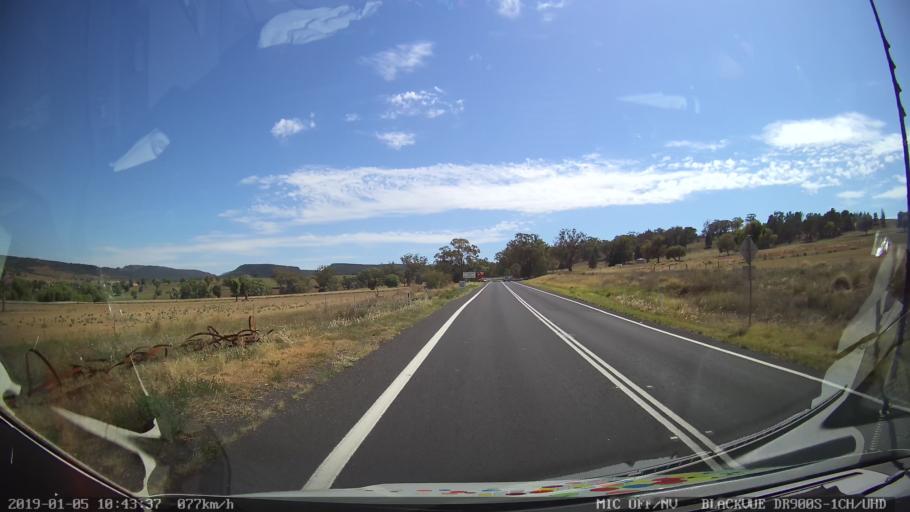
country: AU
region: New South Wales
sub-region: Warrumbungle Shire
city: Coonabarabran
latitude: -31.4627
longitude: 148.9891
